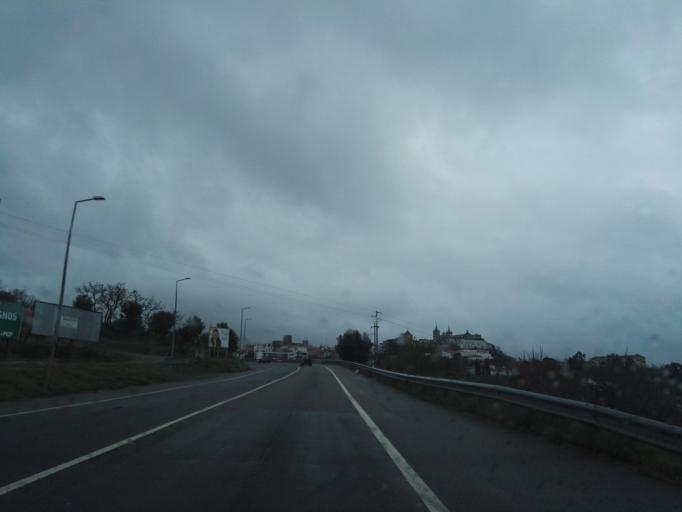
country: PT
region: Portalegre
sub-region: Portalegre
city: Portalegre
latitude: 39.2976
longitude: -7.4363
